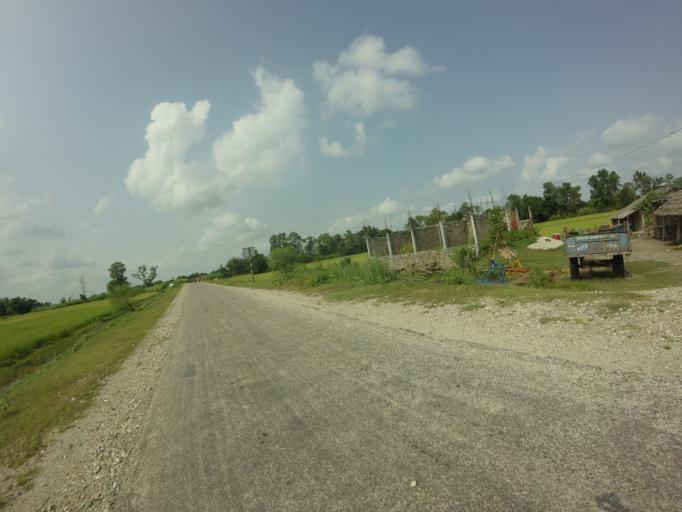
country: NP
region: Far Western
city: Tikapur
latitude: 28.4685
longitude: 81.0748
